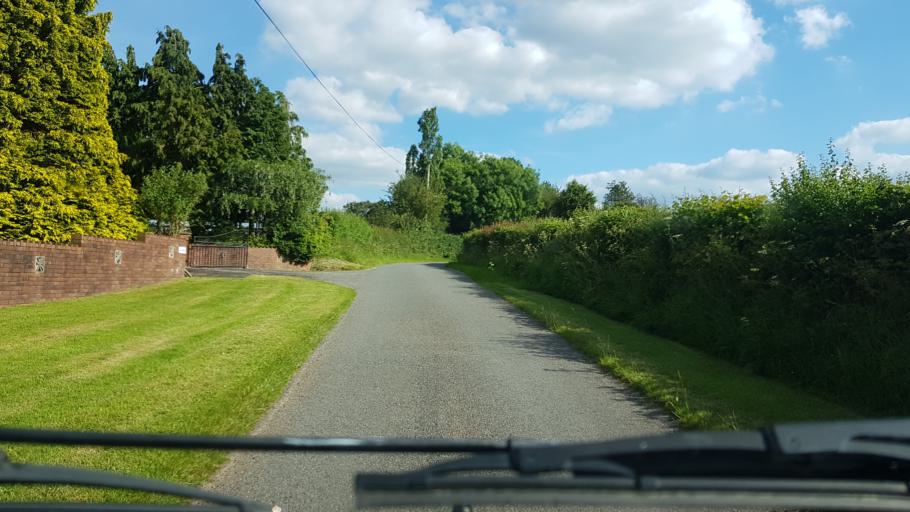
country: GB
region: England
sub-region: Worcestershire
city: Bewdley
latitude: 52.3417
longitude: -2.3304
